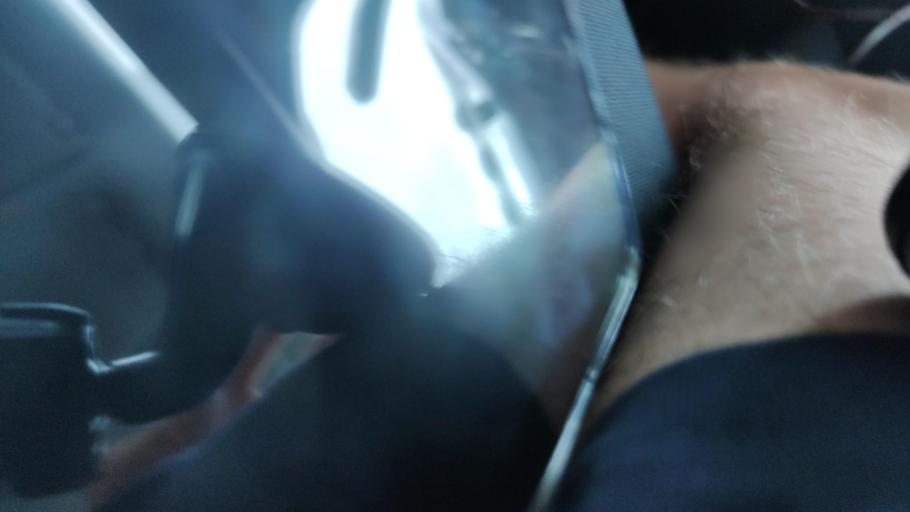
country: DE
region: Baden-Wuerttemberg
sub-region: Freiburg Region
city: Lauf
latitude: 48.6486
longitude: 8.1337
